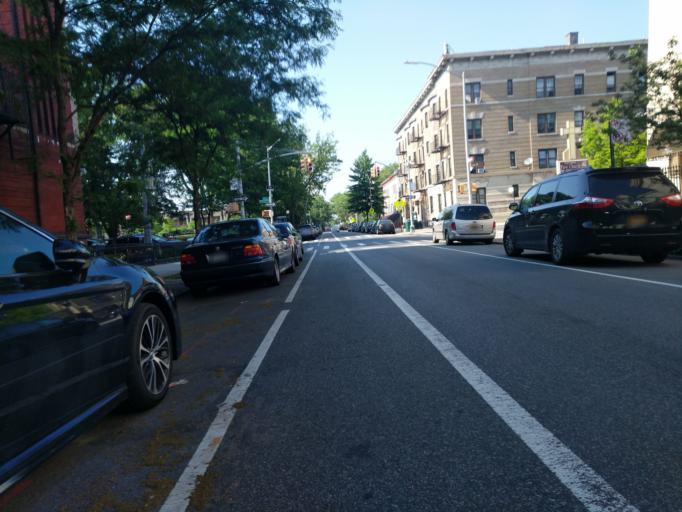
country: US
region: New York
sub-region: Kings County
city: Brooklyn
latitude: 40.6726
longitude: -73.9419
